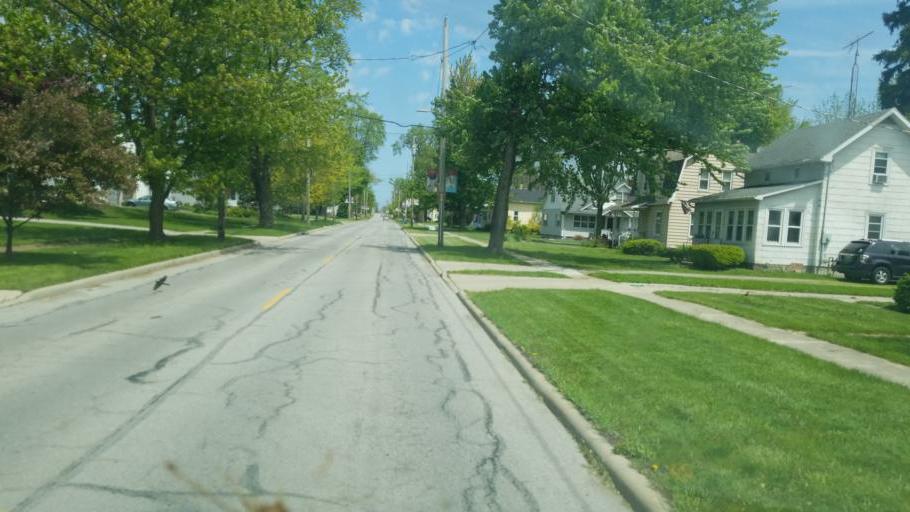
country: US
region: Ohio
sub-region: Ottawa County
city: Oak Harbor
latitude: 41.5147
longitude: -83.1450
